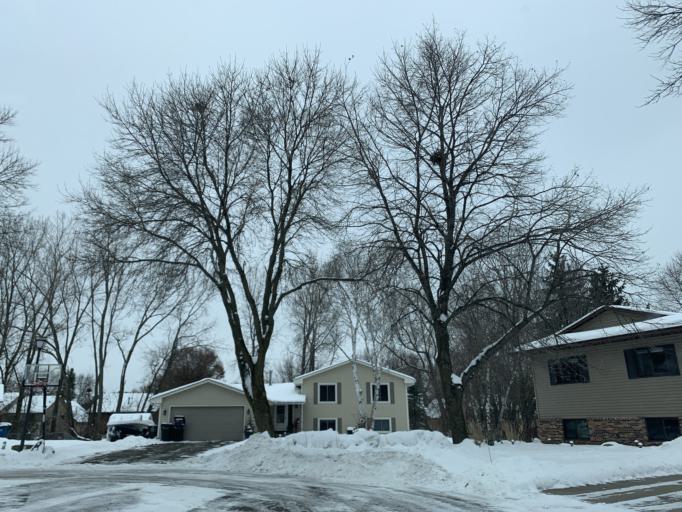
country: US
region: Minnesota
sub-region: Anoka County
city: Coon Rapids
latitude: 45.1604
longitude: -93.3027
